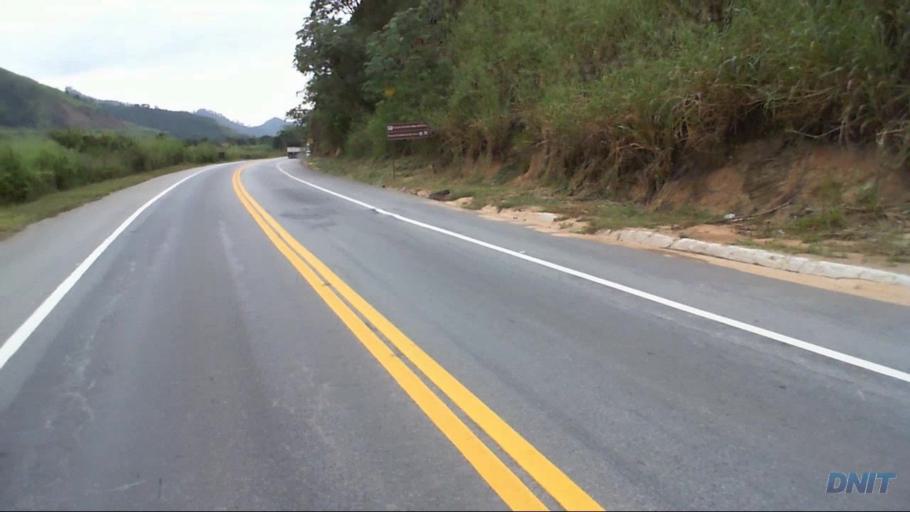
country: BR
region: Minas Gerais
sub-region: Timoteo
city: Timoteo
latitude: -19.6100
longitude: -42.7662
